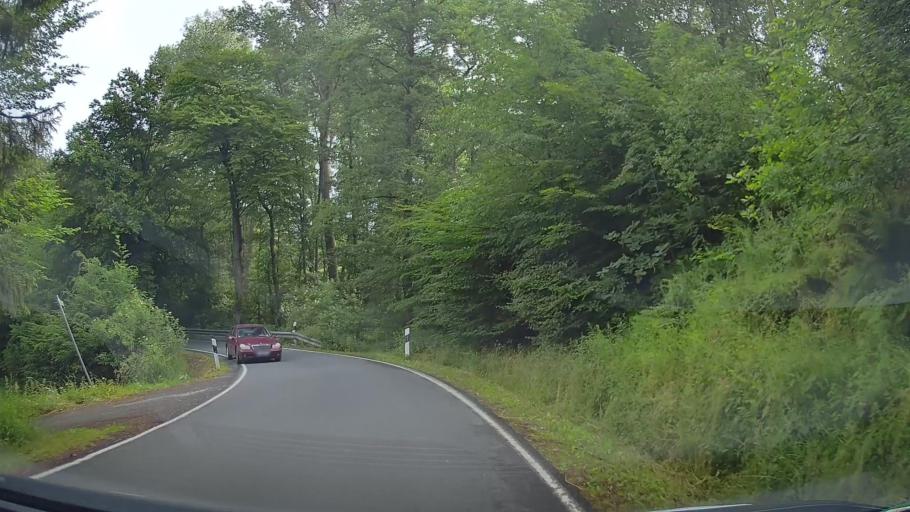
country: DE
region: North Rhine-Westphalia
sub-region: Regierungsbezirk Detmold
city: Barntrup
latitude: 52.0931
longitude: 9.1314
